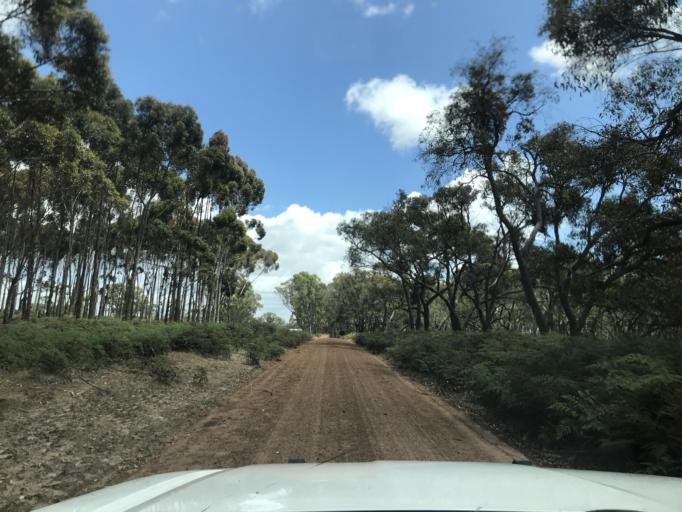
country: AU
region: South Australia
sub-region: Wattle Range
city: Penola
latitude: -37.0750
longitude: 141.3388
